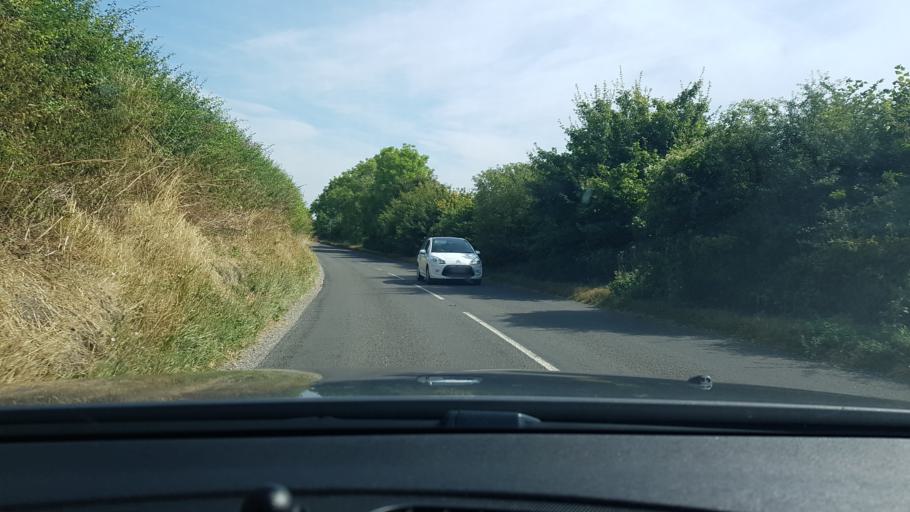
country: GB
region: England
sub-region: Wiltshire
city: Shalbourne
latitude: 51.3637
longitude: -1.5611
